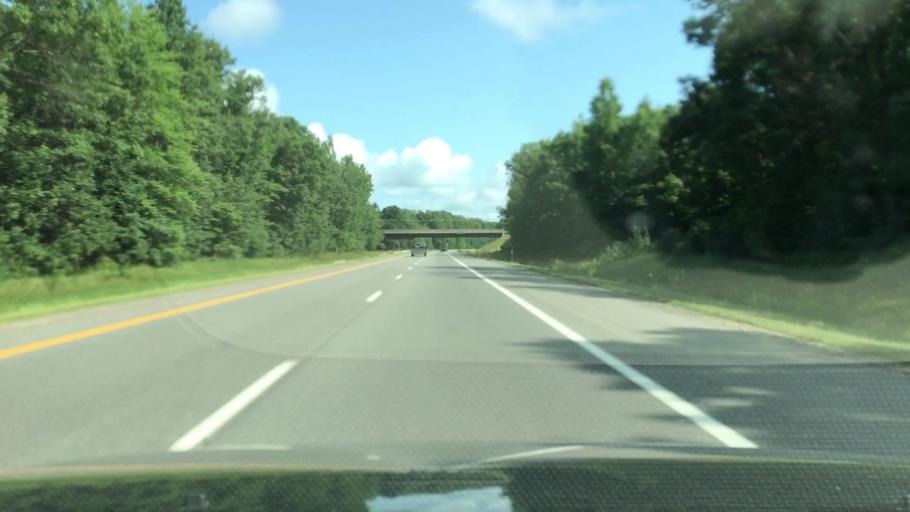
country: US
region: Michigan
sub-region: Montcalm County
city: Howard City
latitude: 43.4366
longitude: -85.4927
